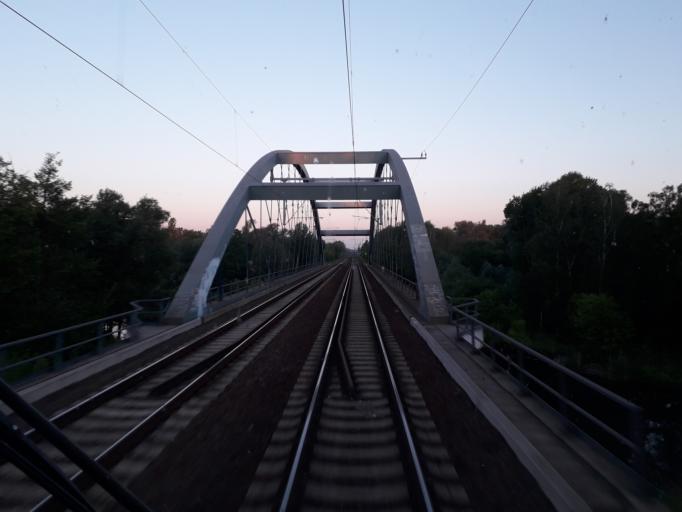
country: DE
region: Brandenburg
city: Hennigsdorf
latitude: 52.6637
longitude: 13.2233
